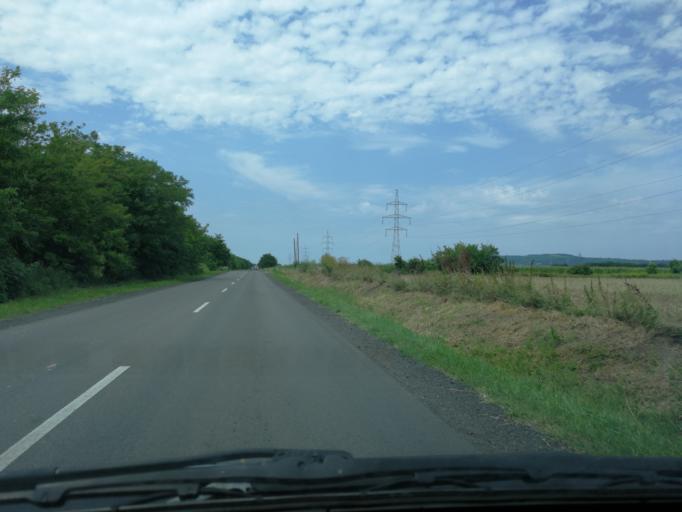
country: HU
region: Baranya
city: Siklos
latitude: 45.8486
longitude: 18.3722
